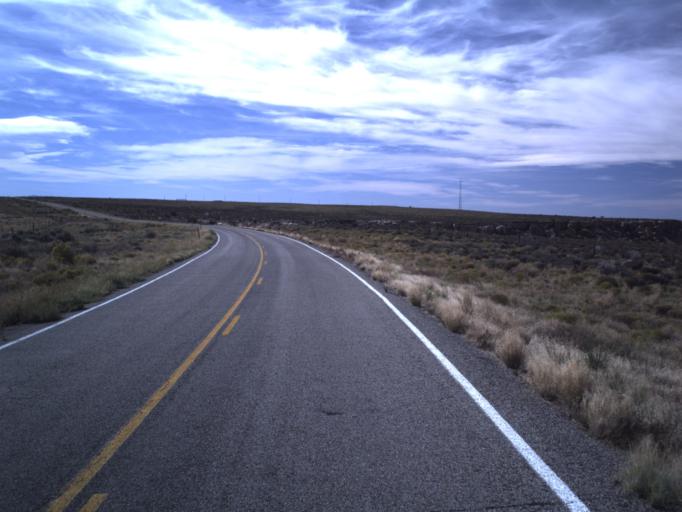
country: US
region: Utah
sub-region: San Juan County
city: Blanding
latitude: 37.3401
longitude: -109.3493
